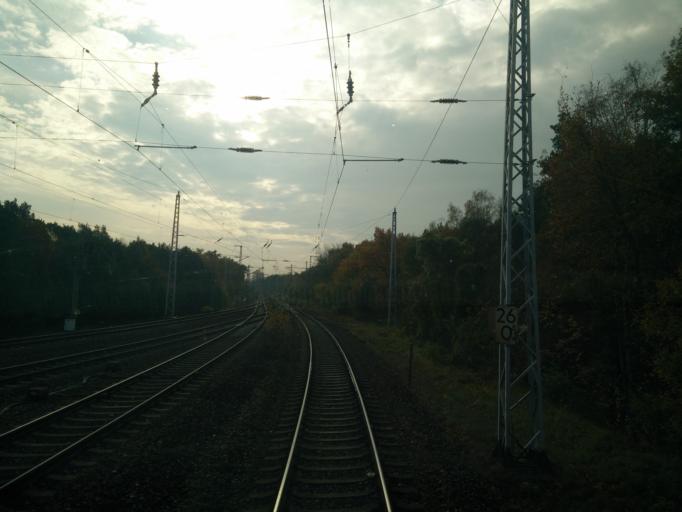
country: DE
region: Berlin
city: Karlshorst
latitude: 52.4650
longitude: 13.5504
